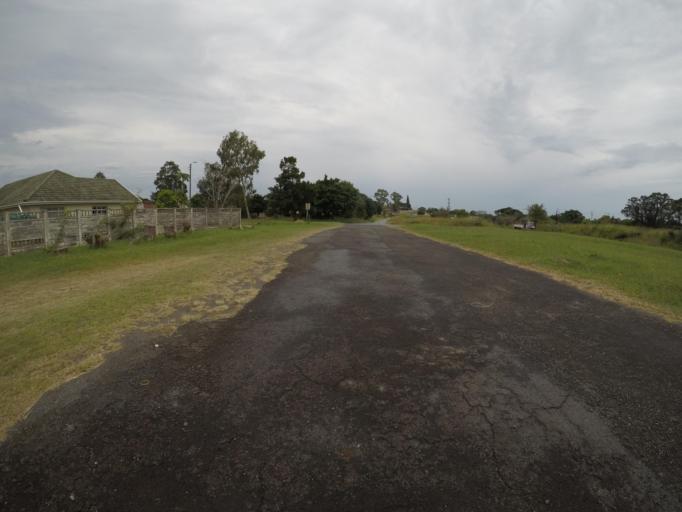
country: ZA
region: Eastern Cape
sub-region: Buffalo City Metropolitan Municipality
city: East London
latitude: -32.9662
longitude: 27.8430
